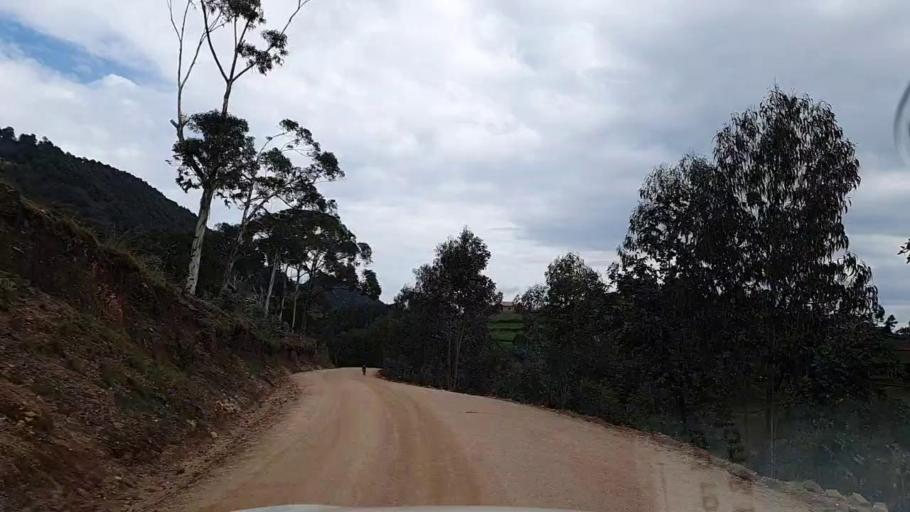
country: RW
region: Southern Province
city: Nzega
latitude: -2.3928
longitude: 29.4519
